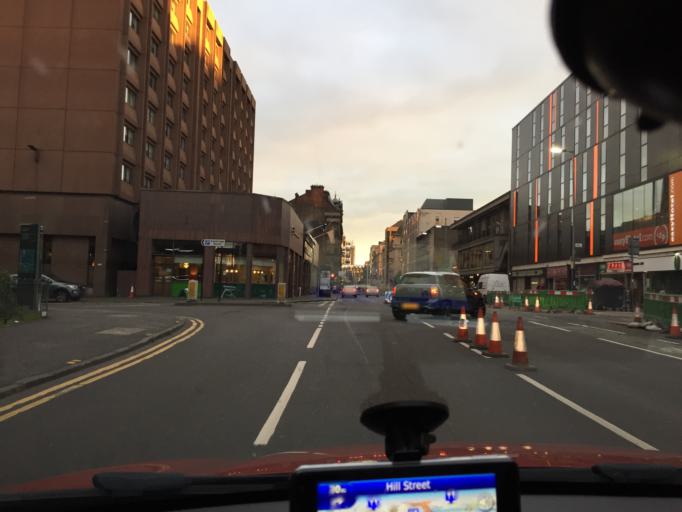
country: GB
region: Scotland
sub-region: Glasgow City
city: Glasgow
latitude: 55.8667
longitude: -4.2596
